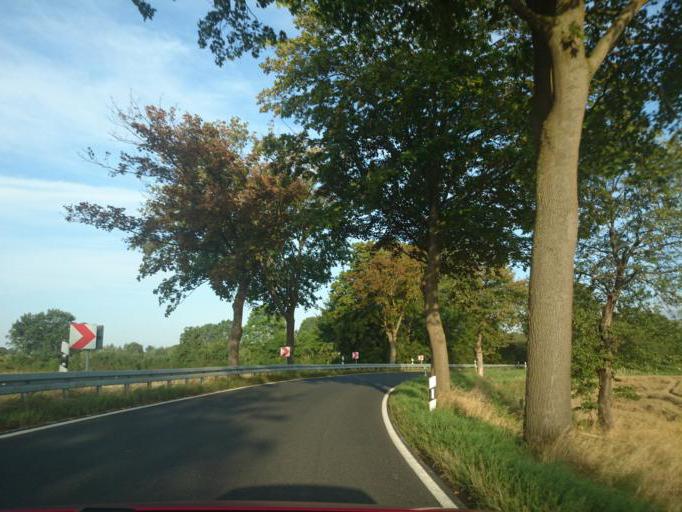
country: DE
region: Mecklenburg-Vorpommern
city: Velgast
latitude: 54.3314
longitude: 12.8035
